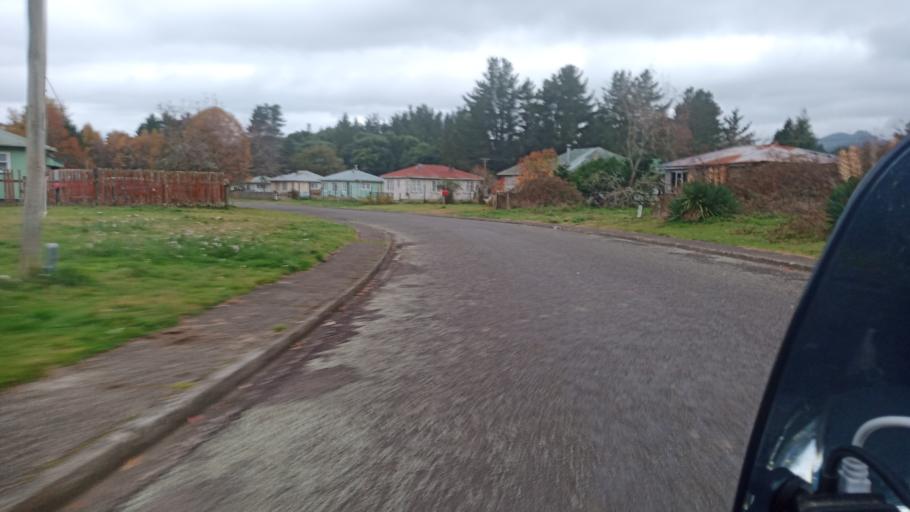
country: NZ
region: Bay of Plenty
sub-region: Whakatane District
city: Murupara
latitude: -38.6415
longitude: 176.7331
